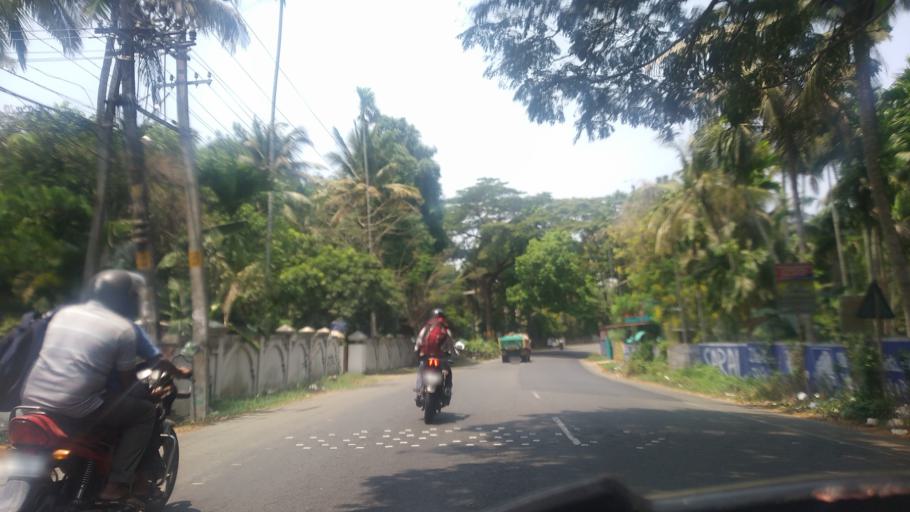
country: IN
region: Kerala
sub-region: Thrissur District
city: Kodungallur
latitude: 10.2490
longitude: 76.1864
